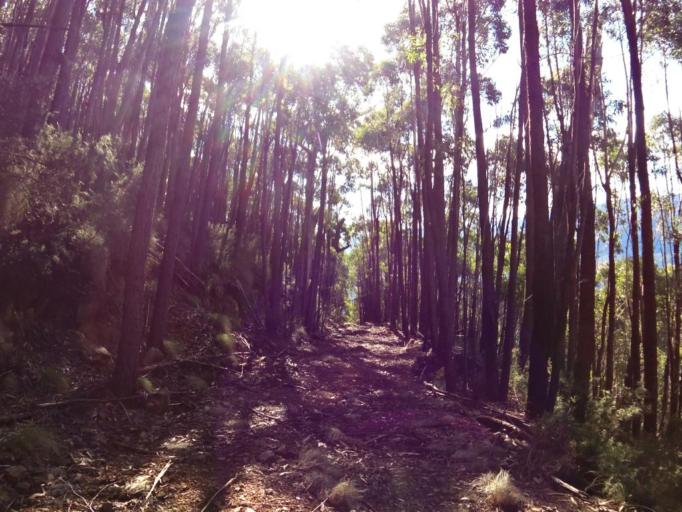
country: AU
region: Victoria
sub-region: Yarra Ranges
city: Millgrove
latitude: -37.7604
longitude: 145.6741
